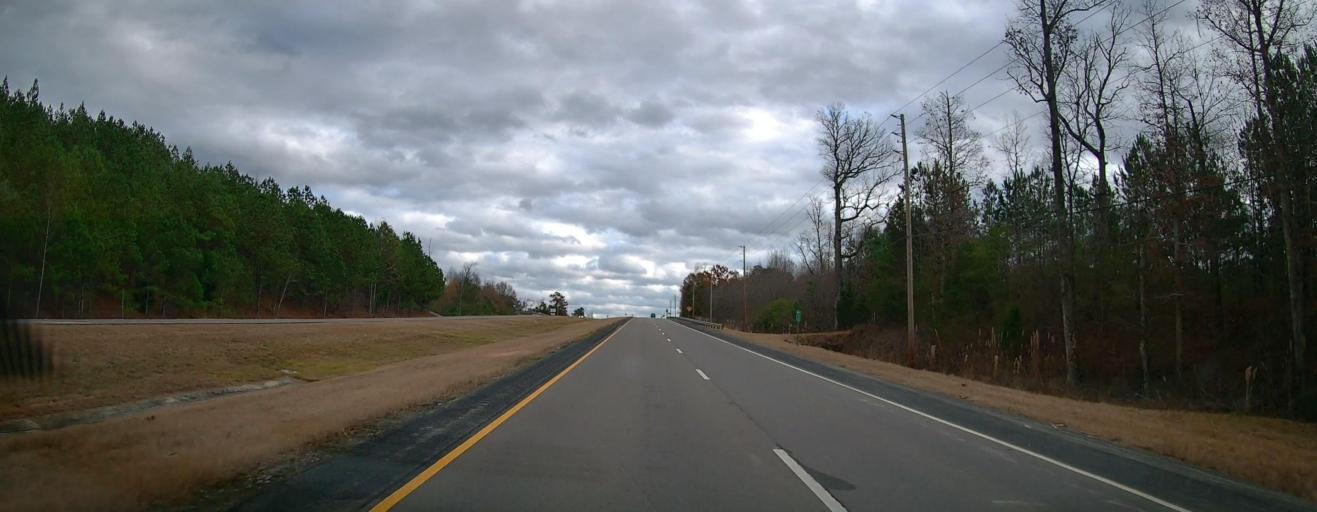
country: US
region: Alabama
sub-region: Morgan County
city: Falkville
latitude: 34.2479
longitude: -86.9650
